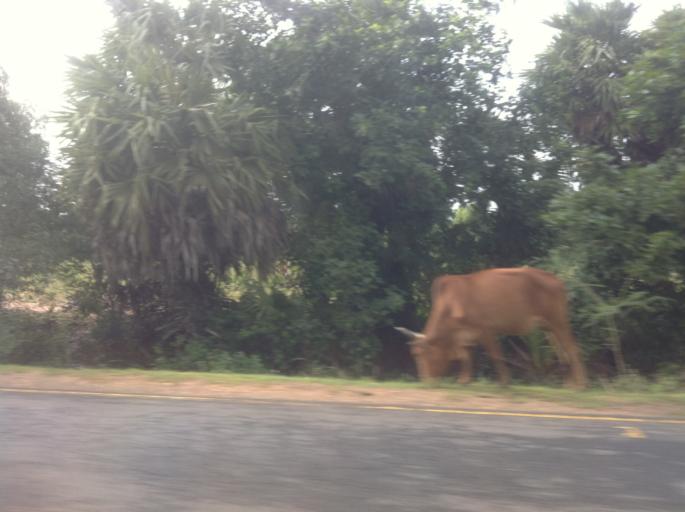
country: IN
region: Tamil Nadu
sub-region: Kancheepuram
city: Cheyyur
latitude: 12.3341
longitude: 80.0443
